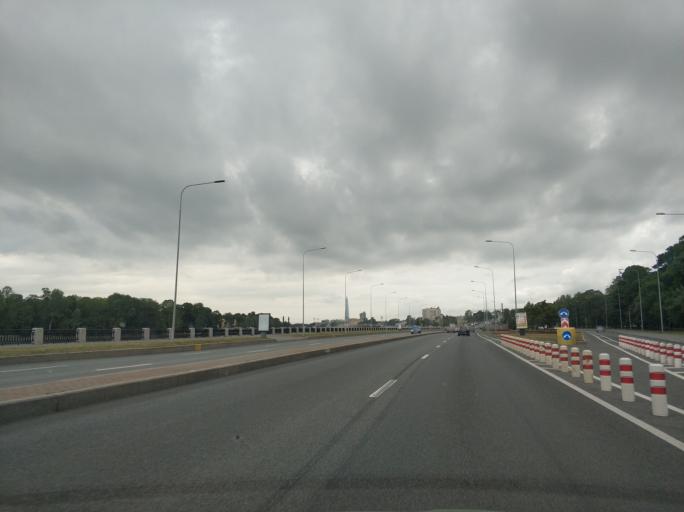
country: RU
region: Leningrad
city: Chernaya Rechka
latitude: 59.9822
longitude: 30.3094
